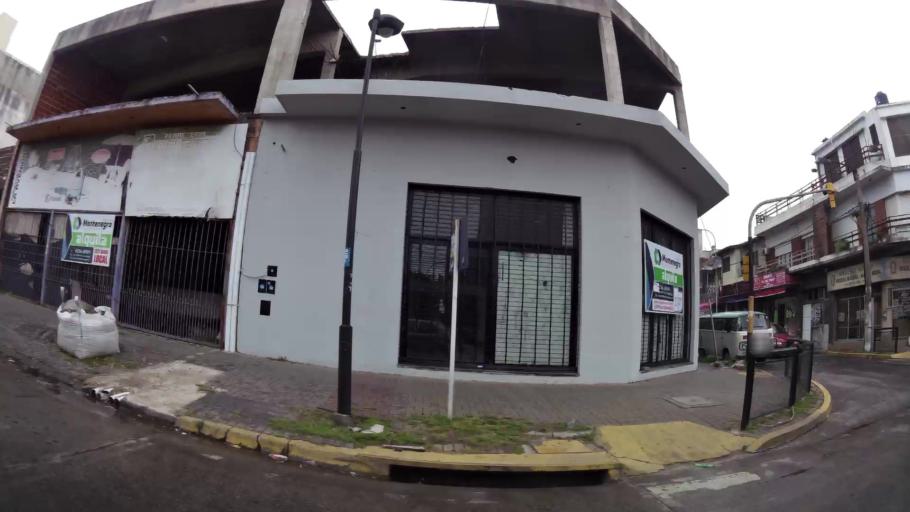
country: AR
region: Buenos Aires
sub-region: Partido de Quilmes
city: Quilmes
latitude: -34.7569
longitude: -58.2079
